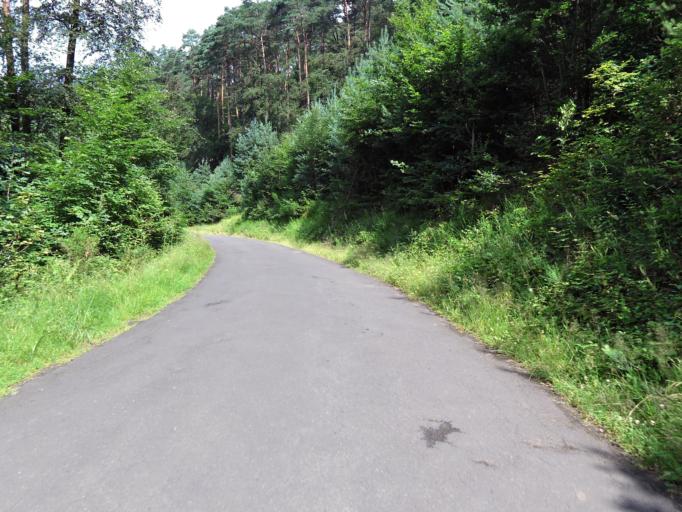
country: DE
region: Rheinland-Pfalz
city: Carlsberg
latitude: 49.4512
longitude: 8.0523
